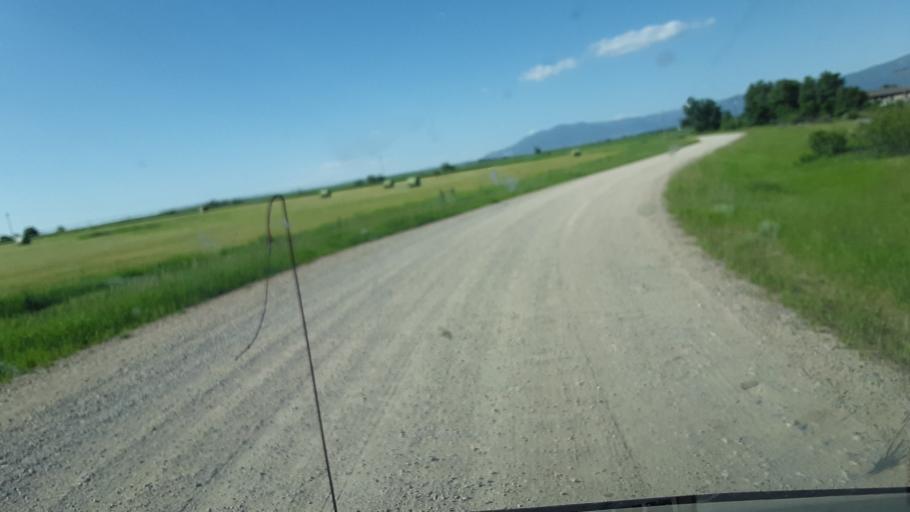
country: US
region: Montana
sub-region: Carbon County
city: Red Lodge
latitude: 45.3510
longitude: -109.1595
